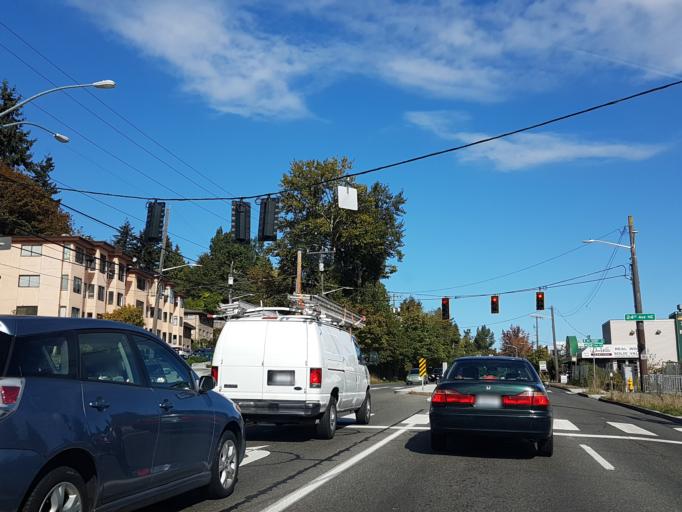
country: US
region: Washington
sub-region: King County
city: Lake Forest Park
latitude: 47.7044
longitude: -122.3016
